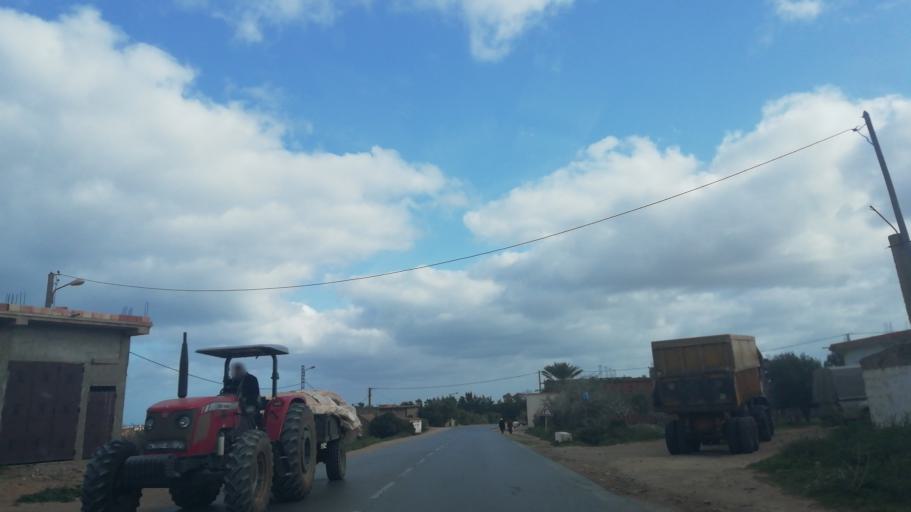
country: DZ
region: Relizane
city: Mazouna
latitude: 36.2780
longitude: 0.6371
